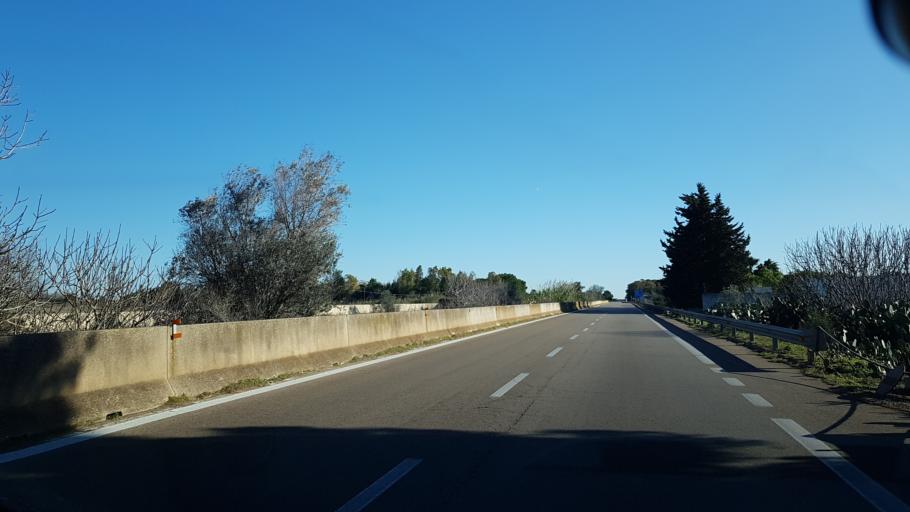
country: IT
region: Apulia
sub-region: Provincia di Lecce
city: Alezio
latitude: 40.0307
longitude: 18.0307
